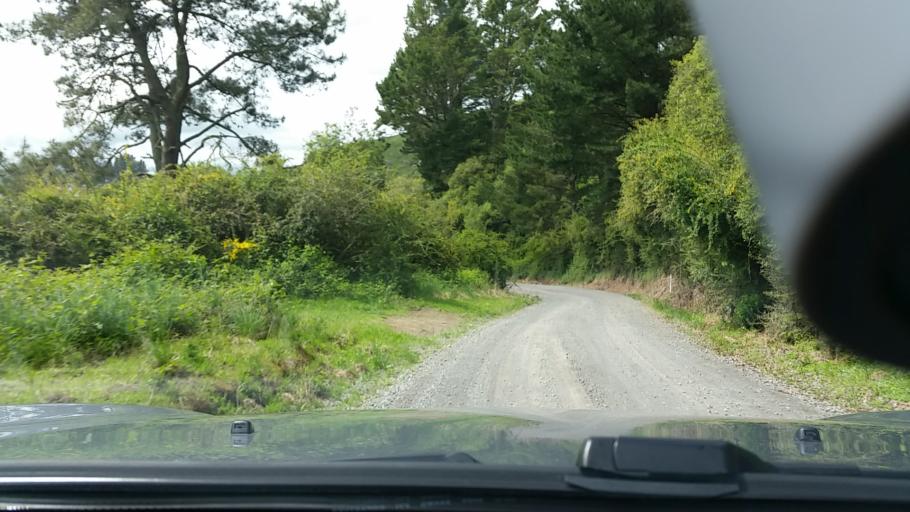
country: NZ
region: Bay of Plenty
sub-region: Rotorua District
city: Rotorua
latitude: -38.3875
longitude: 176.1707
